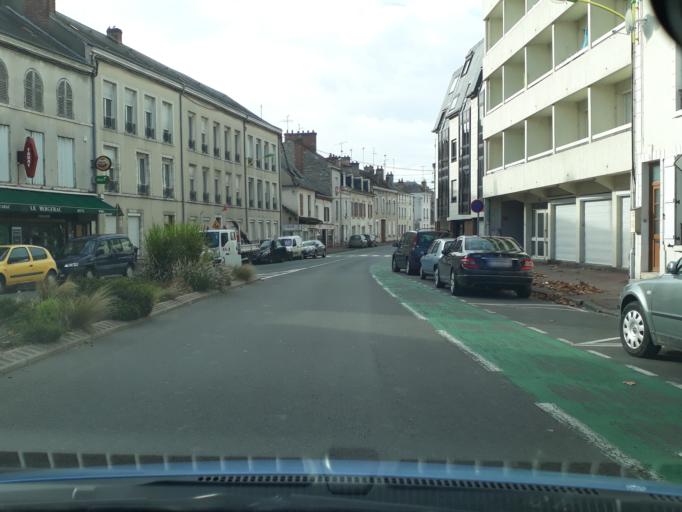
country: FR
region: Centre
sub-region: Departement du Loiret
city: Pithiviers
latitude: 48.1714
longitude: 2.2542
